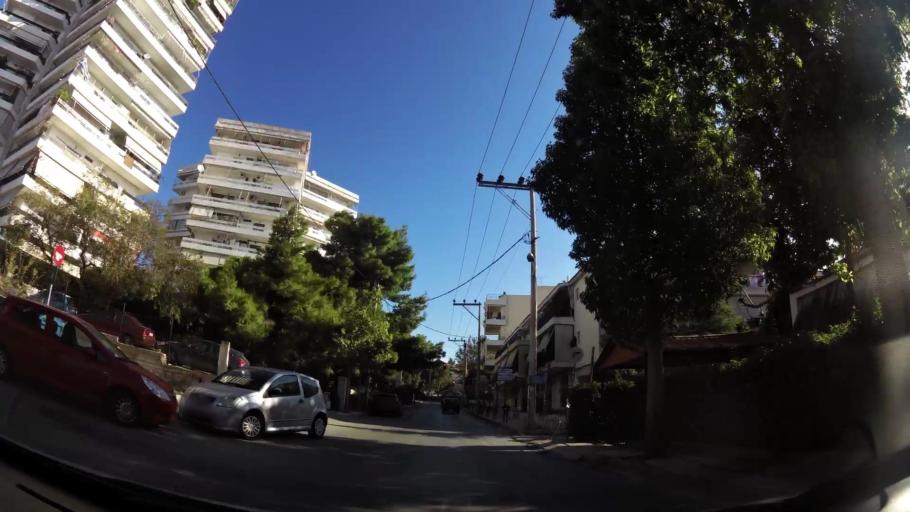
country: GR
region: Attica
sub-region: Nomarchia Athinas
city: Lykovrysi
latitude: 38.0554
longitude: 23.7785
